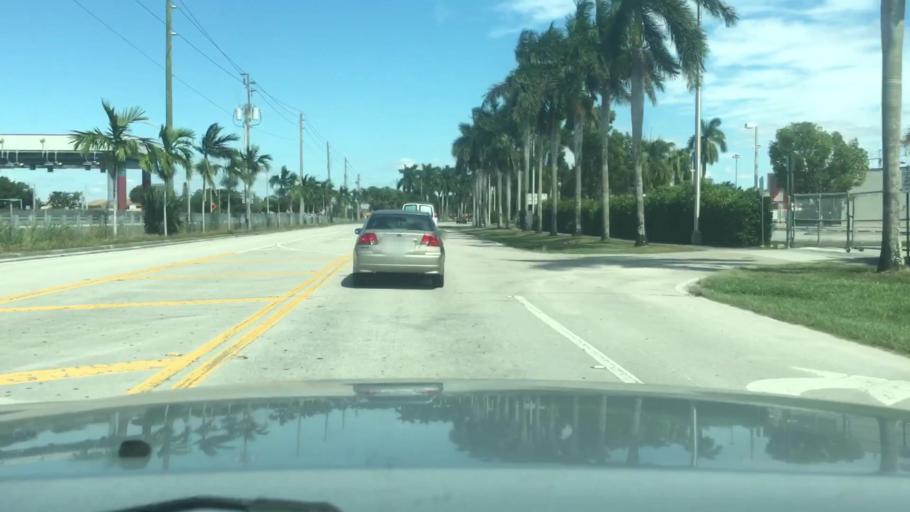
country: US
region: Florida
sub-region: Miami-Dade County
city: Sweetwater
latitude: 25.7588
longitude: -80.3829
